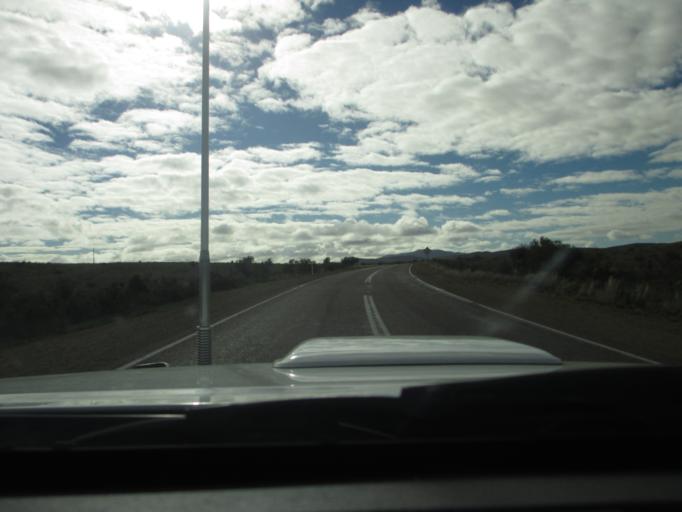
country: AU
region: South Australia
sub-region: Flinders Ranges
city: Quorn
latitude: -32.3280
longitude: 138.4762
